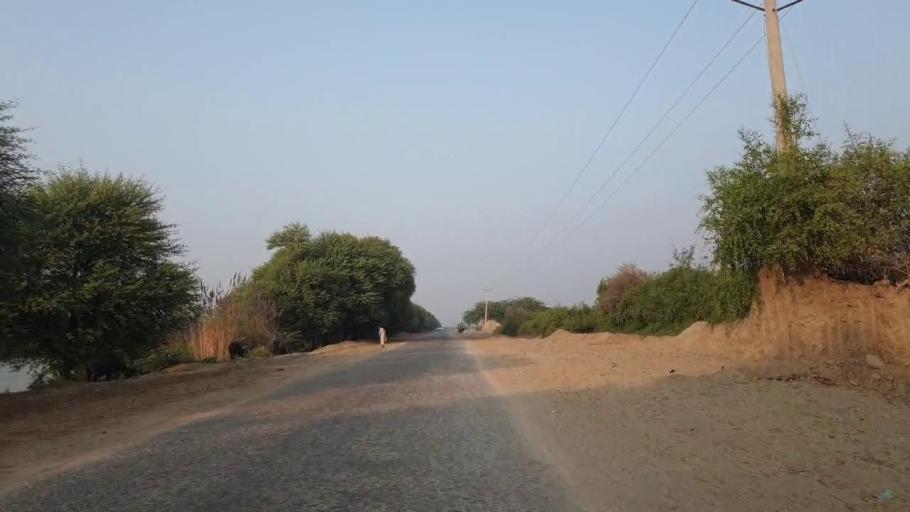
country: PK
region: Sindh
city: Tando Muhammad Khan
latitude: 25.1270
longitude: 68.4320
